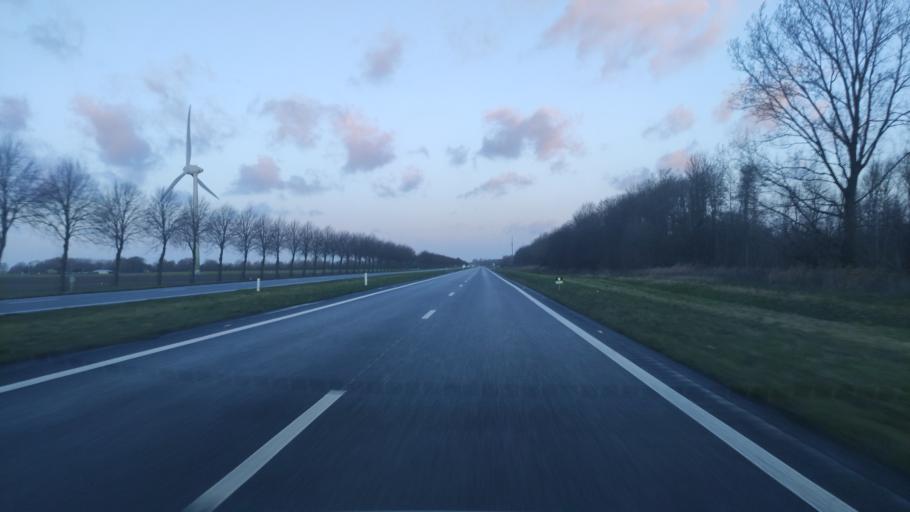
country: NL
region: Gelderland
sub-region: Gemeente Harderwijk
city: Harderwijk
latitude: 52.4286
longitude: 5.5719
